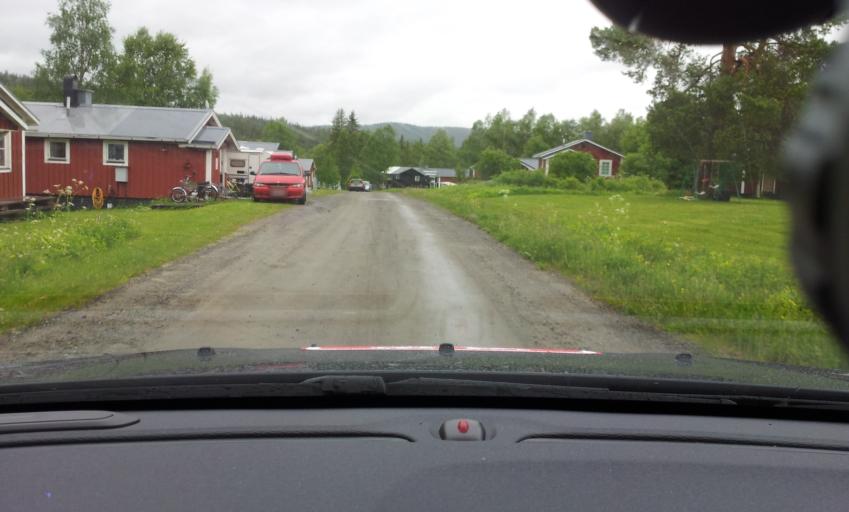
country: SE
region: Jaemtland
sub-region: Are Kommun
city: Are
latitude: 63.5092
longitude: 12.6877
